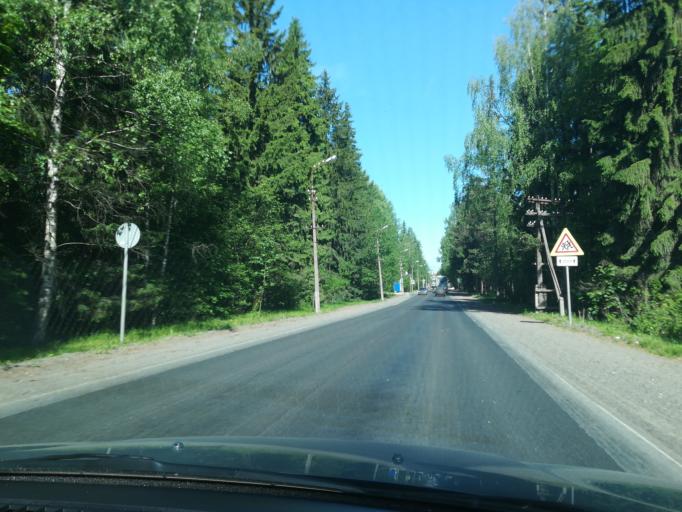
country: RU
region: Leningrad
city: Svetogorsk
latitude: 61.1023
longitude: 28.8706
